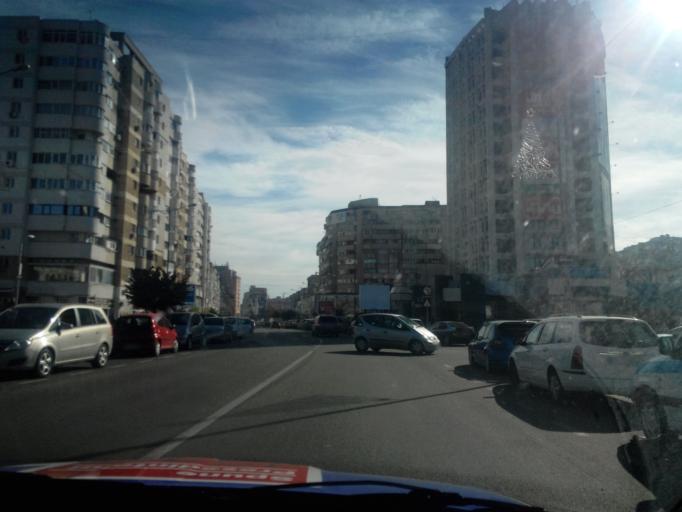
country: RO
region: Bacau
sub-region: Municipiul Bacau
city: Bacau
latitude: 46.5692
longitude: 26.9118
